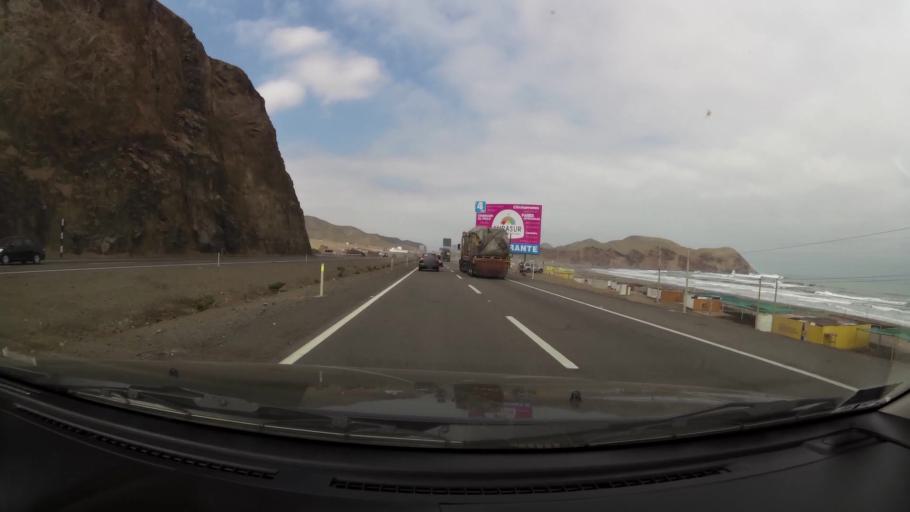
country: PE
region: Lima
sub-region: Provincia de Canete
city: Mala
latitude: -12.6395
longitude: -76.6691
